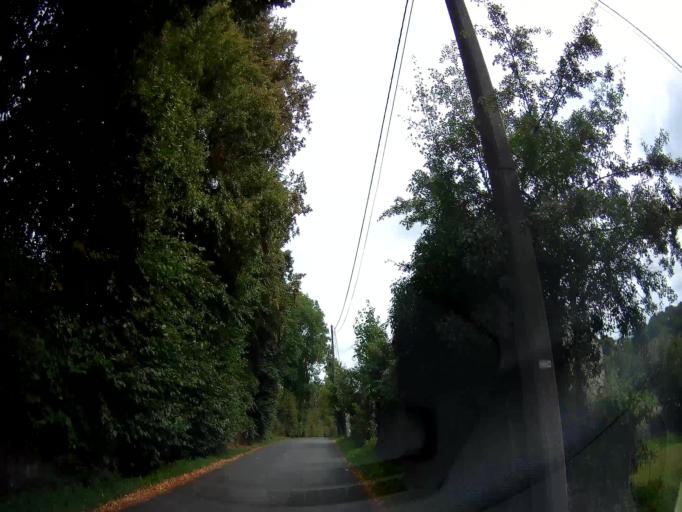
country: BE
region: Wallonia
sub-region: Province de Liege
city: Marchin
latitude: 50.4443
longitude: 5.2628
